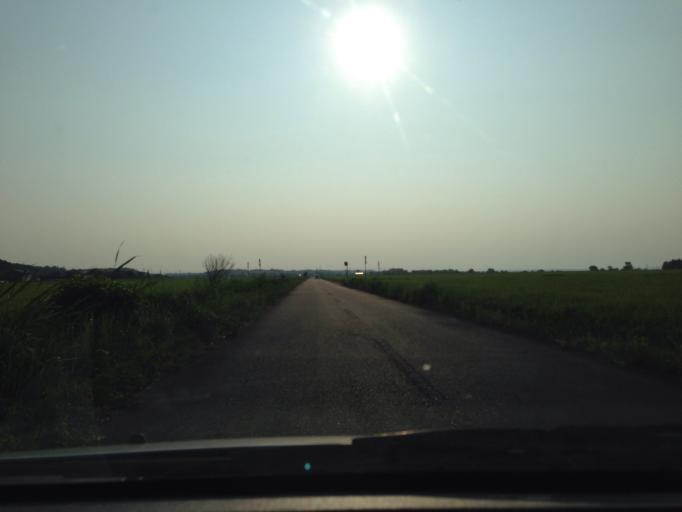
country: JP
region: Ibaraki
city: Inashiki
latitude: 36.0253
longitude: 140.3133
